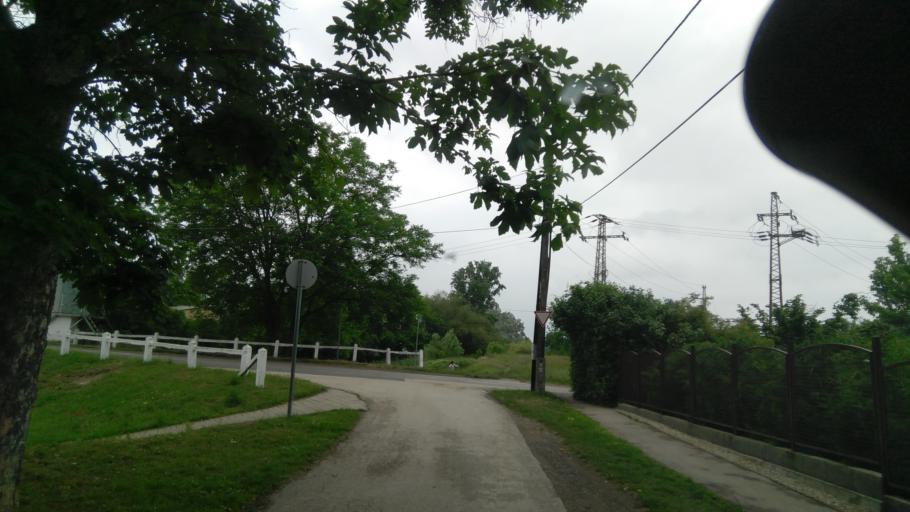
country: HU
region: Bekes
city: Bekescsaba
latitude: 46.6906
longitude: 21.0960
